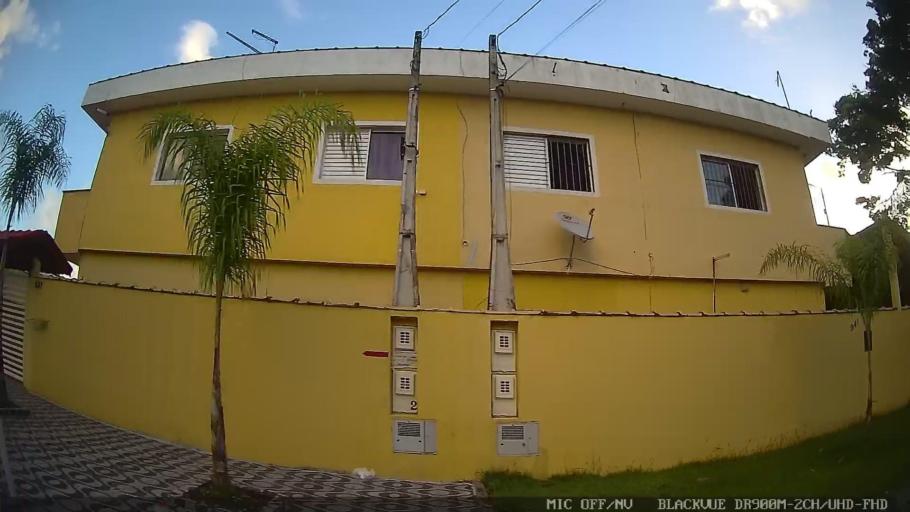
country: BR
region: Sao Paulo
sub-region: Itanhaem
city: Itanhaem
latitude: -24.1440
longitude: -46.7280
